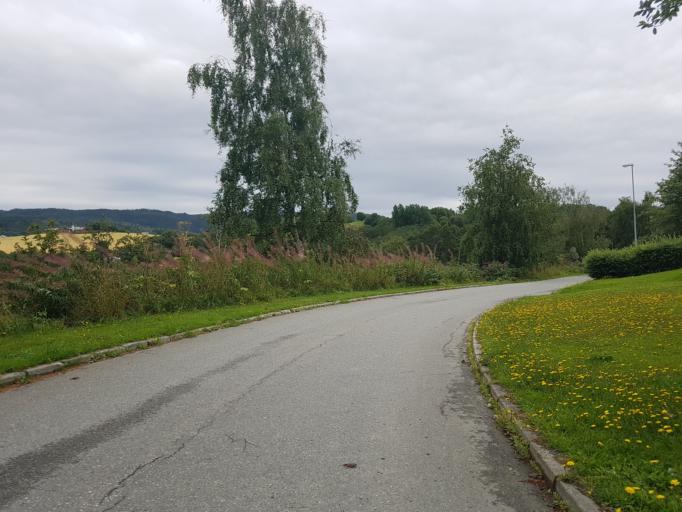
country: NO
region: Sor-Trondelag
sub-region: Trondheim
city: Trondheim
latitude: 63.3863
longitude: 10.4029
